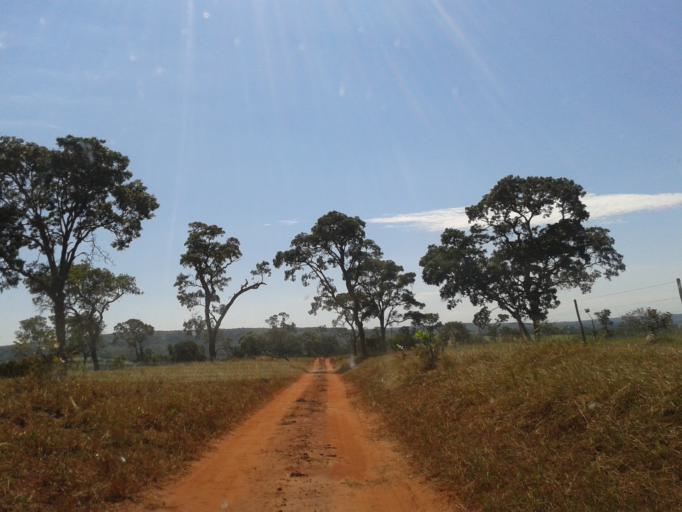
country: BR
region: Minas Gerais
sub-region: Campina Verde
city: Campina Verde
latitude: -19.4013
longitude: -49.7658
